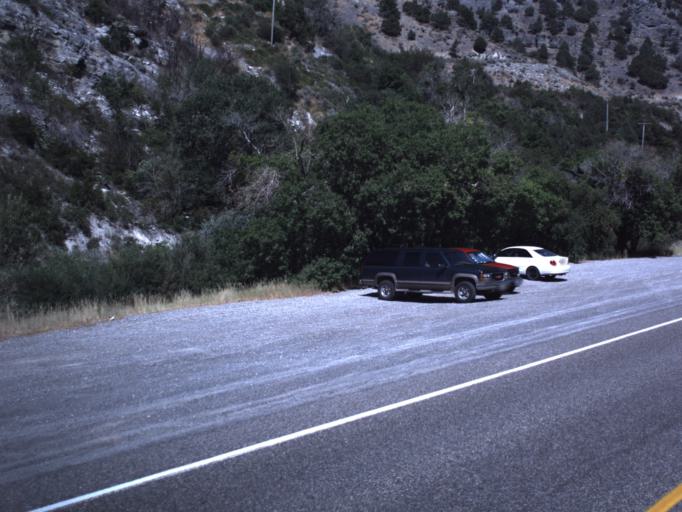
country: US
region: Utah
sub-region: Cache County
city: North Logan
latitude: 41.7425
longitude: -111.7813
